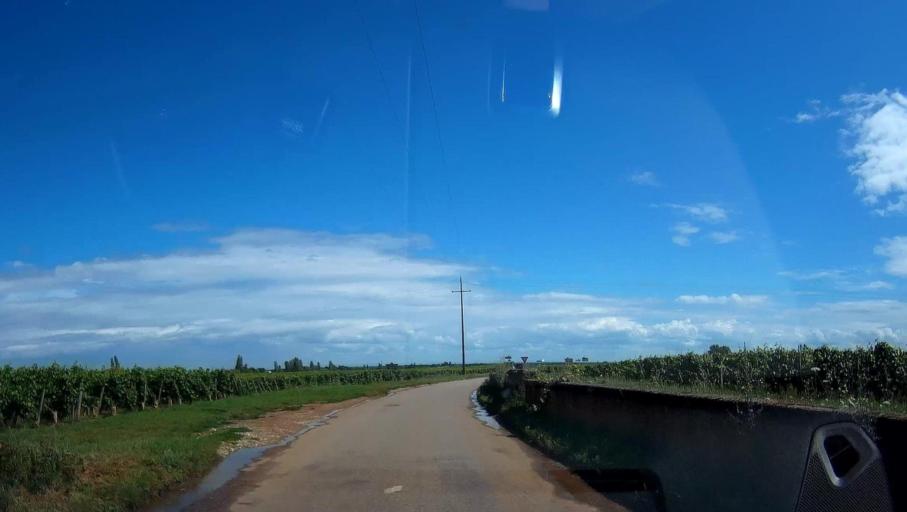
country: FR
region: Bourgogne
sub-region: Departement de la Cote-d'Or
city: Bligny-les-Beaune
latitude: 47.0034
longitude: 4.7990
